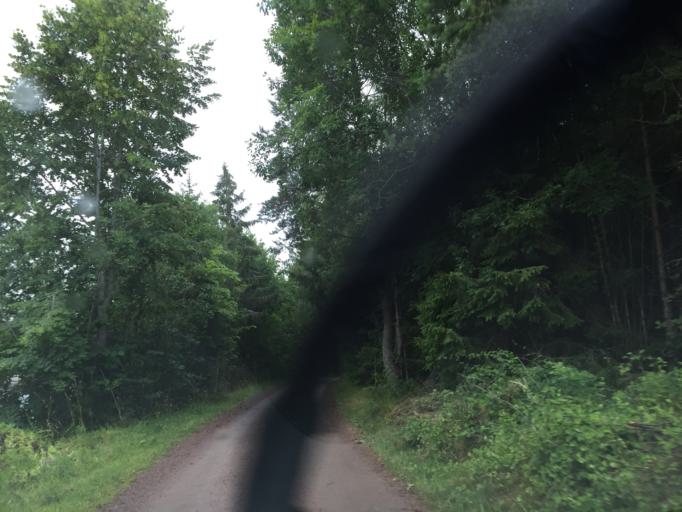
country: SE
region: OEstergoetland
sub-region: Vadstena Kommun
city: Vadstena
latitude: 58.4752
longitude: 14.8298
